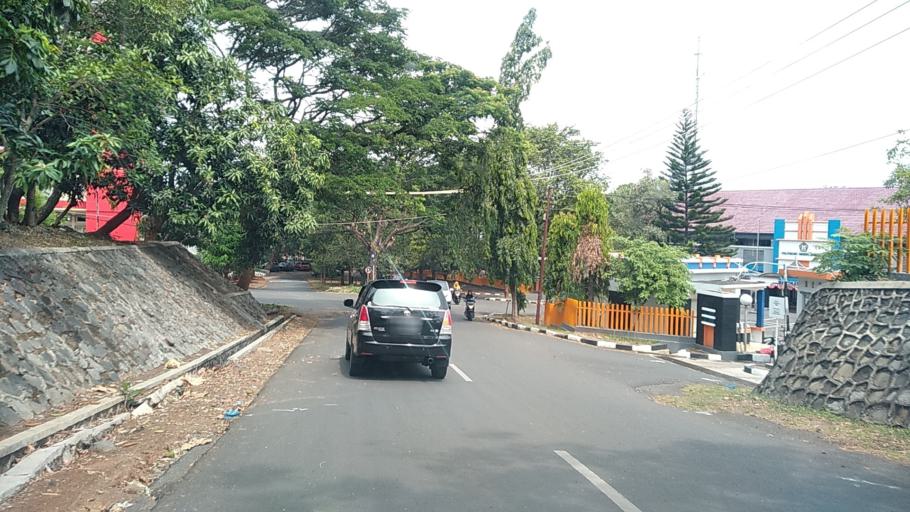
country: ID
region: Central Java
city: Semarang
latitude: -7.0514
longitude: 110.4351
